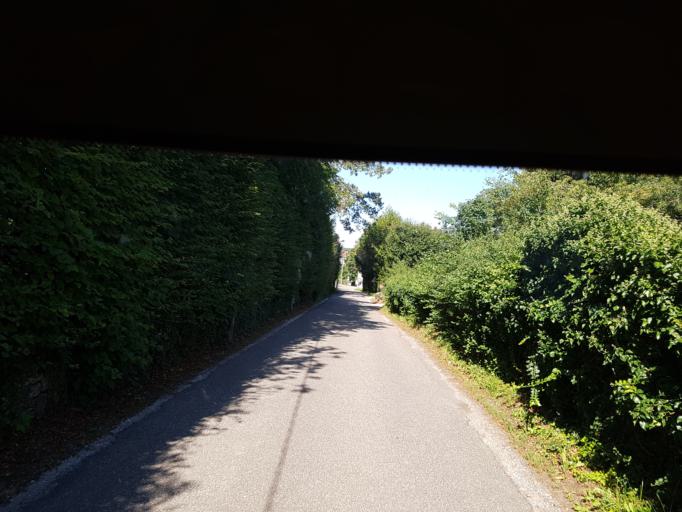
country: FR
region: Franche-Comte
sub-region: Departement du Jura
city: Perrigny
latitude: 46.7287
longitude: 5.5856
